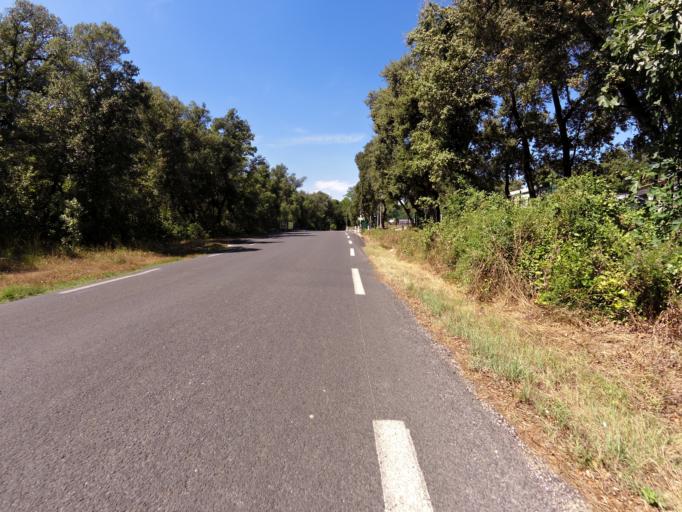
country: FR
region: Languedoc-Roussillon
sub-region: Departement de l'Herault
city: Boisseron
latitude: 43.7653
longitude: 4.0974
